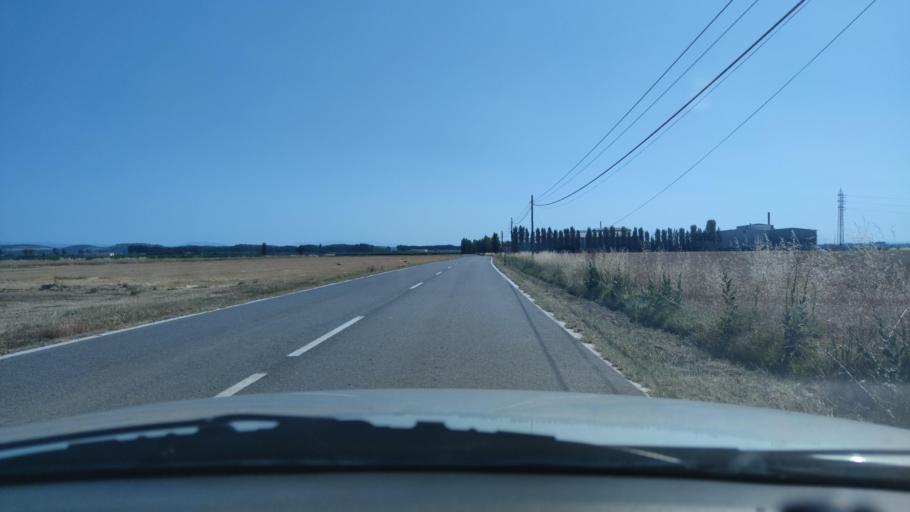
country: ES
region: Catalonia
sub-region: Provincia de Lleida
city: Linyola
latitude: 41.7166
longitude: 0.9110
